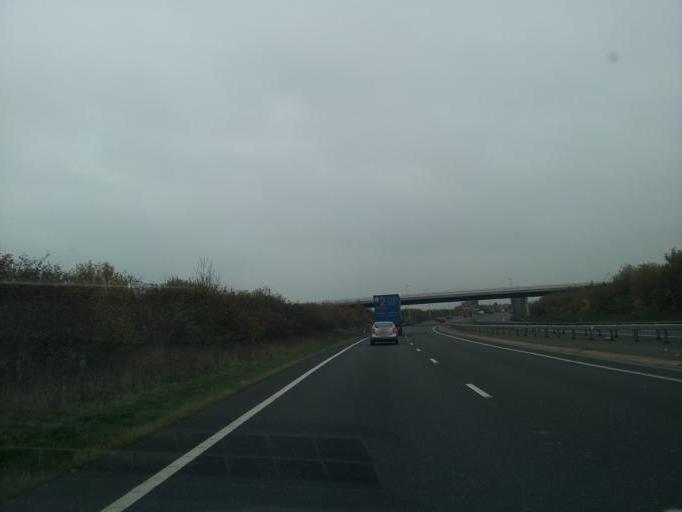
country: GB
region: England
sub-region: Bedford
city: Roxton
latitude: 52.1842
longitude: -0.3146
